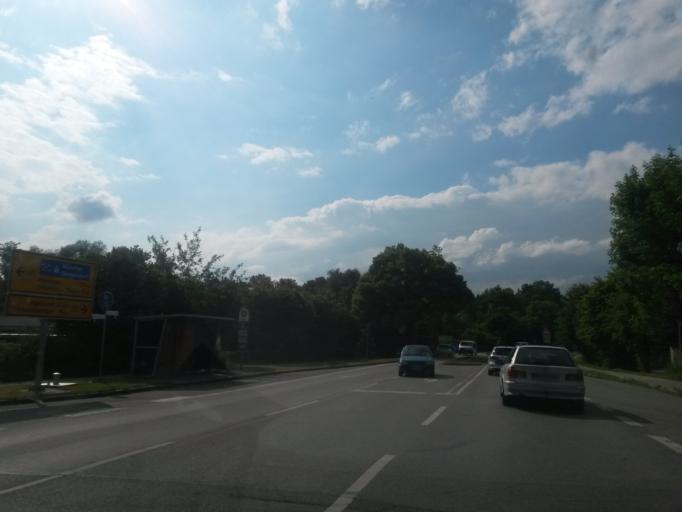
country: DE
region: Bavaria
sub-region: Upper Bavaria
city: Fahrenzhausen
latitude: 48.3433
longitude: 11.5706
